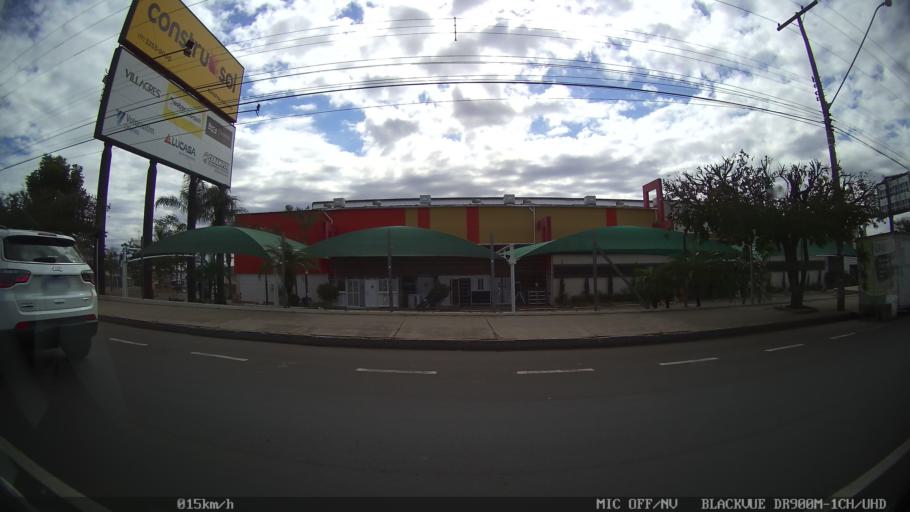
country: BR
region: Sao Paulo
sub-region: Bady Bassitt
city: Bady Bassitt
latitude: -20.8079
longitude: -49.5048
